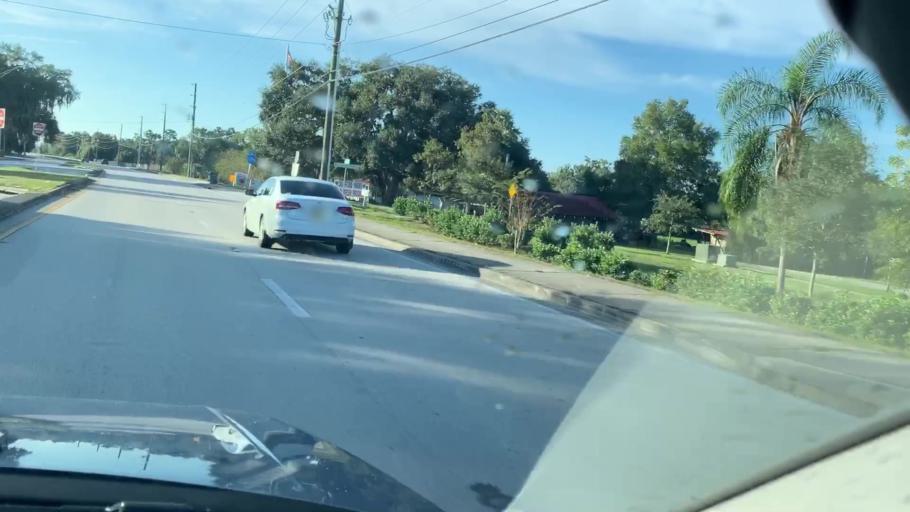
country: US
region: Florida
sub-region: Polk County
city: Gibsonia
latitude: 28.0901
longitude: -81.9965
